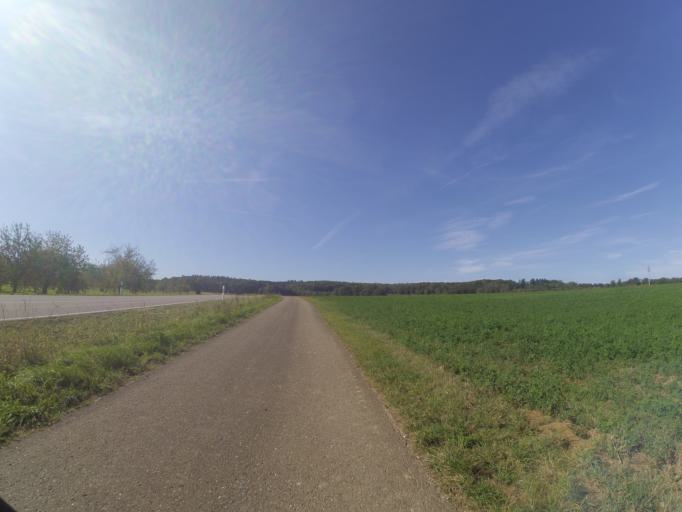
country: DE
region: Baden-Wuerttemberg
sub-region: Tuebingen Region
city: Nerenstetten
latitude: 48.5210
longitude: 10.0913
